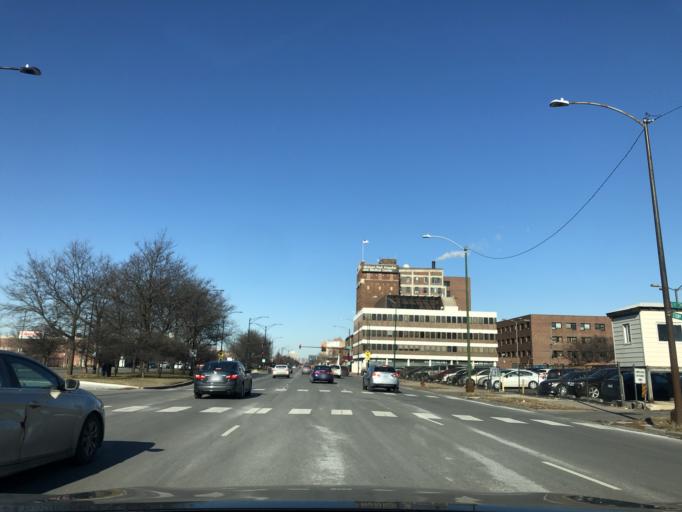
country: US
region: Illinois
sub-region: Cook County
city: Chicago
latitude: 41.7557
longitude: -87.5856
